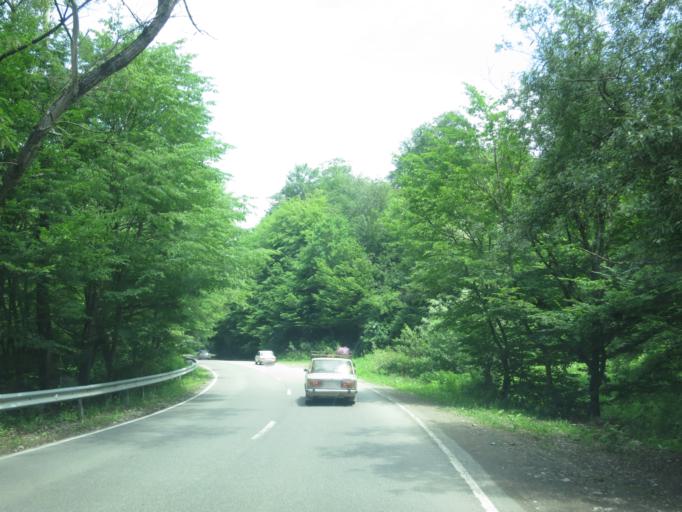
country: GE
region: Kakheti
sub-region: Telavi
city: Telavi
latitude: 41.8754
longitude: 45.3554
